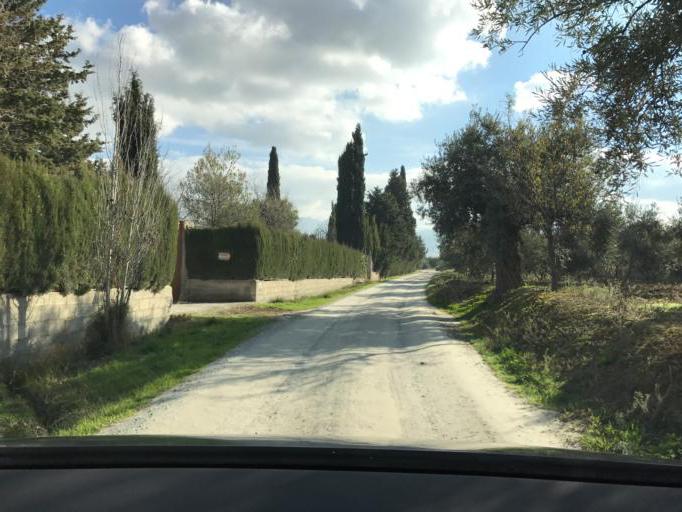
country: ES
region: Andalusia
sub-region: Provincia de Granada
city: Alhendin
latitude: 37.1111
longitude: -3.6289
